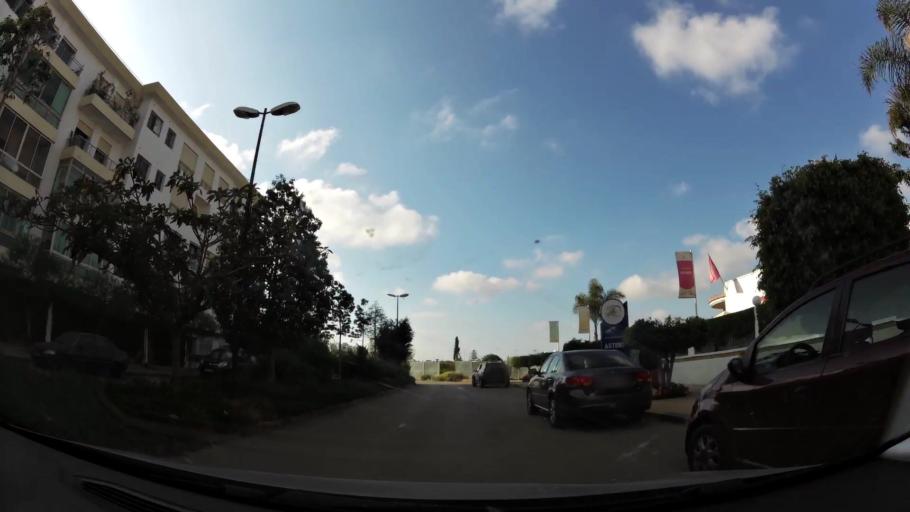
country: MA
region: Rabat-Sale-Zemmour-Zaer
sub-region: Skhirate-Temara
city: Temara
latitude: 33.9525
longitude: -6.8590
